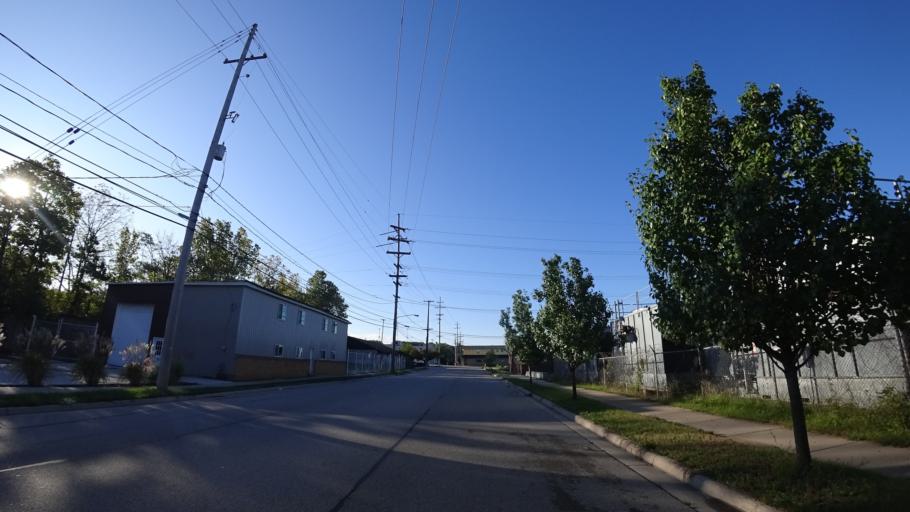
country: US
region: Michigan
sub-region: Kent County
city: Grand Rapids
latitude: 42.9859
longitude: -85.6687
